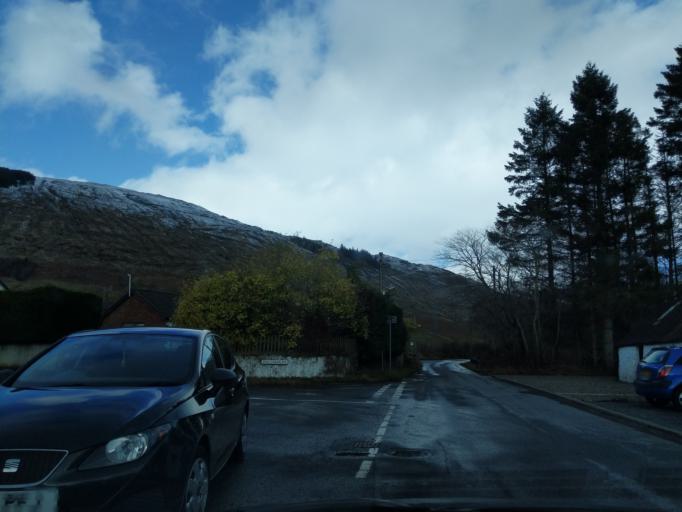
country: GB
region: Scotland
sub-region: Perth and Kinross
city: Comrie
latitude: 56.5775
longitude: -4.0822
